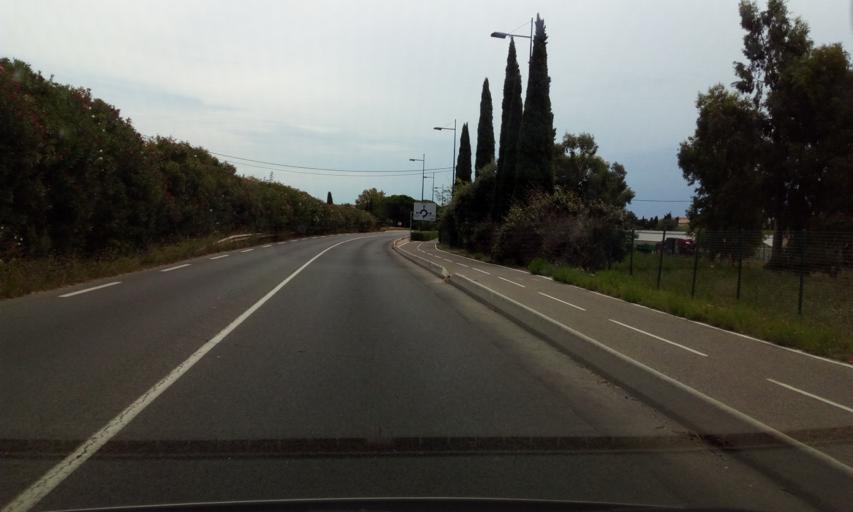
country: FR
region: Provence-Alpes-Cote d'Azur
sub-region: Departement du Var
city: Carqueiranne
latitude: 43.0980
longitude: 6.0666
